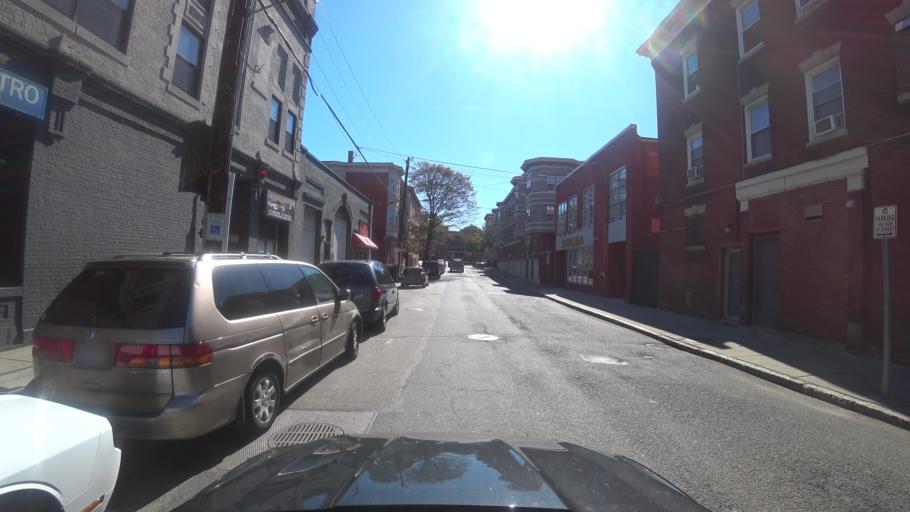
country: US
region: Massachusetts
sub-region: Suffolk County
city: Chelsea
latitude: 42.3917
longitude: -71.0359
